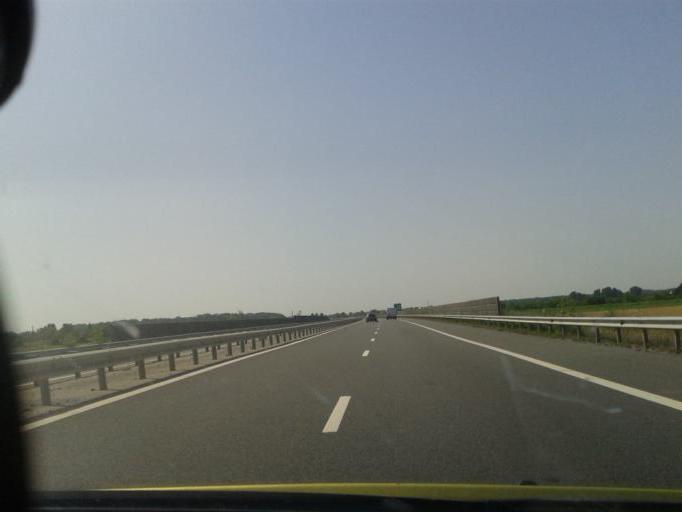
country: RO
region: Prahova
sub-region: Comuna Rafov
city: Rafov
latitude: 44.8767
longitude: 26.1372
